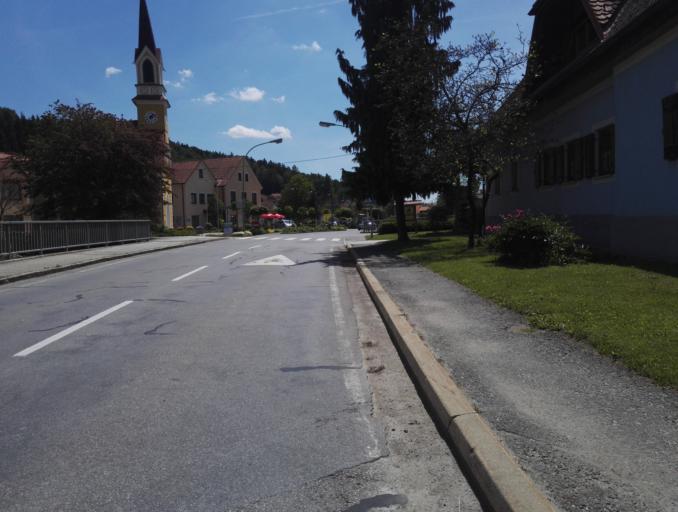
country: AT
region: Styria
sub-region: Politischer Bezirk Graz-Umgebung
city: Grambach
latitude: 47.0143
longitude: 15.5029
